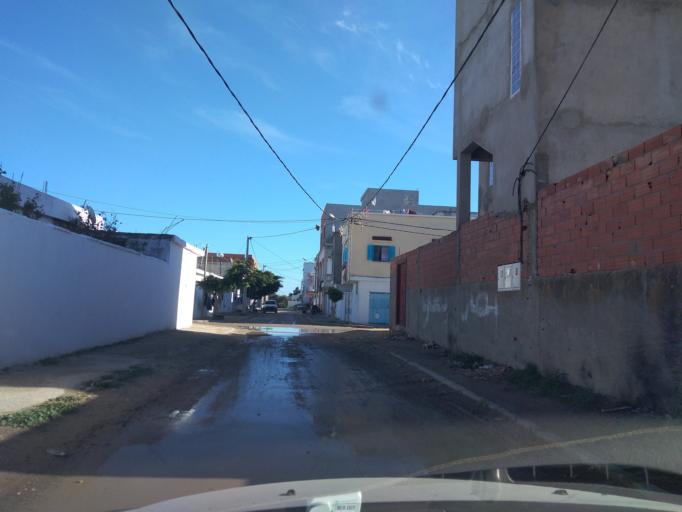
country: TN
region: Ariana
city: Qal'at al Andalus
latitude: 37.0624
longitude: 10.1240
